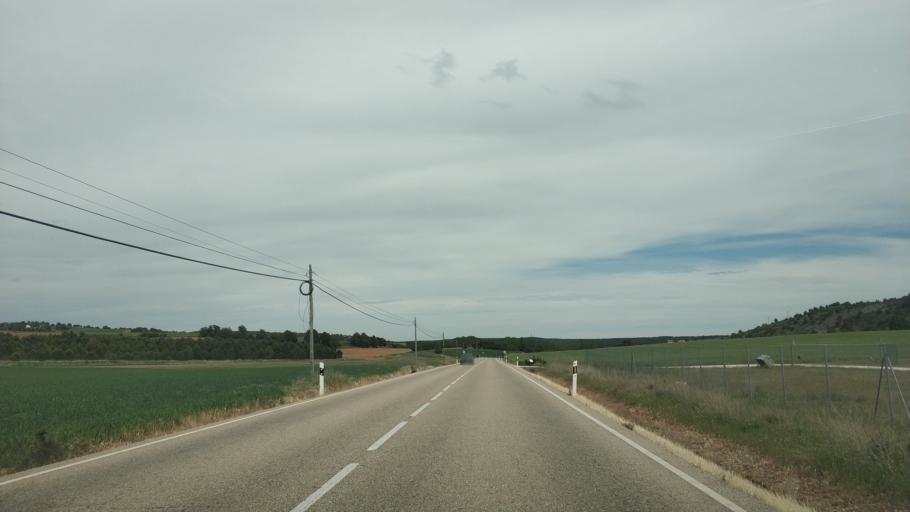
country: ES
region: Castille and Leon
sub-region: Provincia de Soria
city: El Burgo de Osma
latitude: 41.5753
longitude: -3.0235
